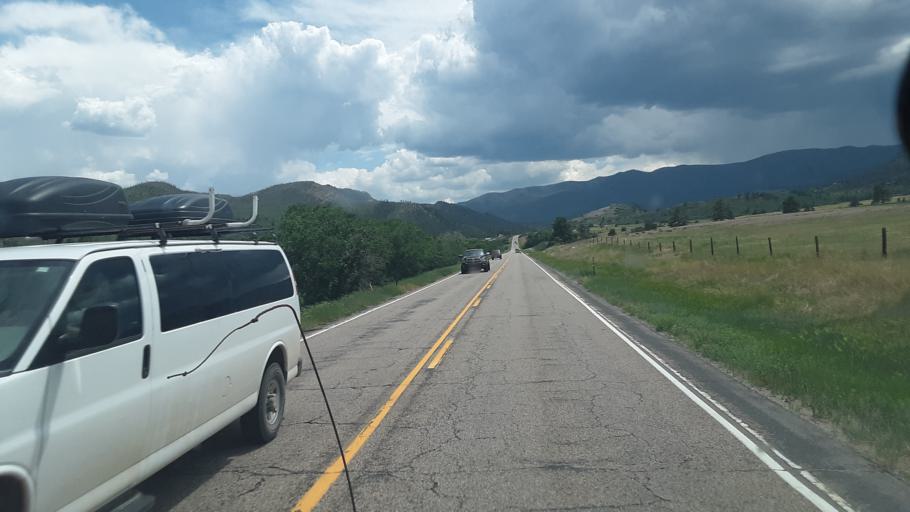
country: US
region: Colorado
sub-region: Fremont County
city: Florence
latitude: 38.2256
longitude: -105.0917
